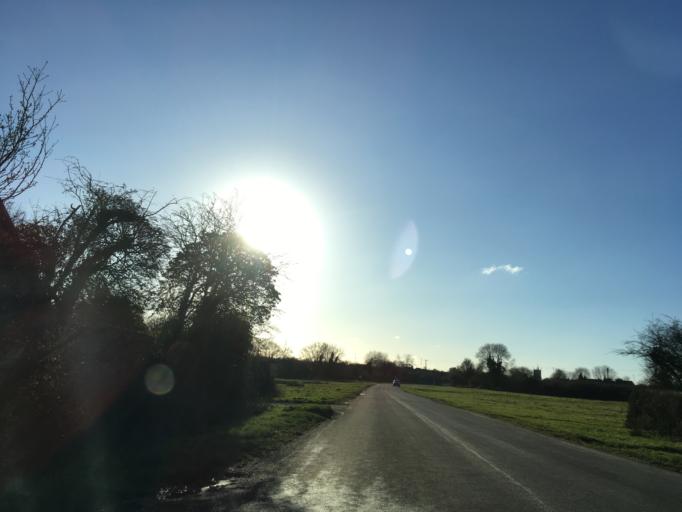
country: GB
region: England
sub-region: South Gloucestershire
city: Chipping Sodbury
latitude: 51.5443
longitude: -2.3843
